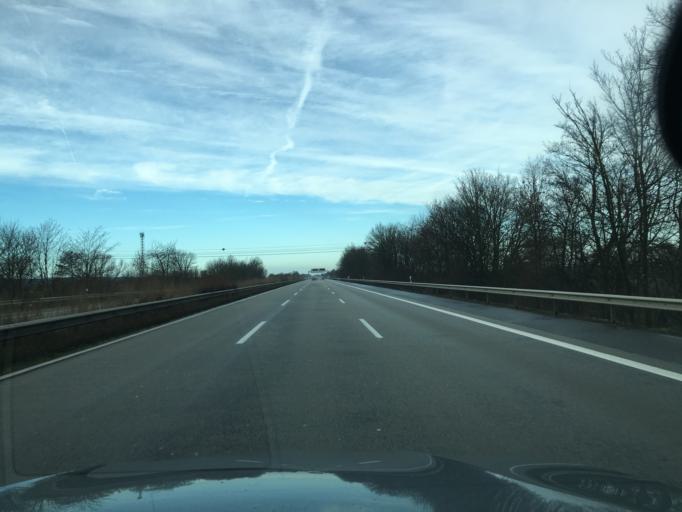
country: DE
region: Rheinland-Pfalz
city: Dernau
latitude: 50.5797
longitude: 7.0665
